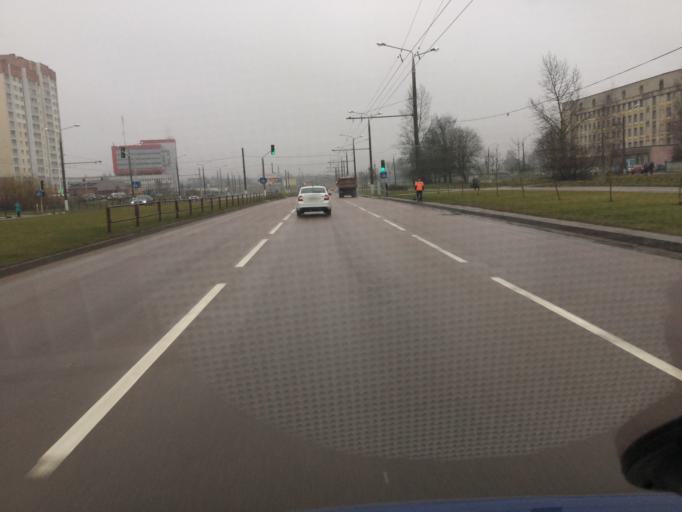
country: BY
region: Vitebsk
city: Vitebsk
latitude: 55.1596
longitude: 30.2285
